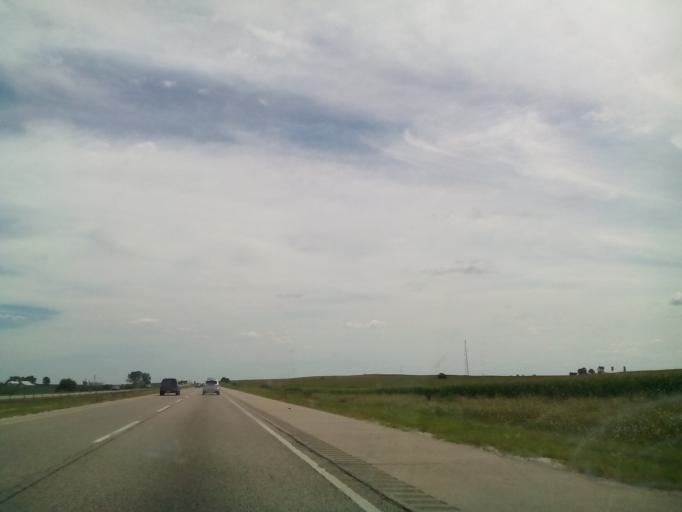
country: US
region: Illinois
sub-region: Kane County
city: Maple Park
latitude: 41.8926
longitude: -88.6368
